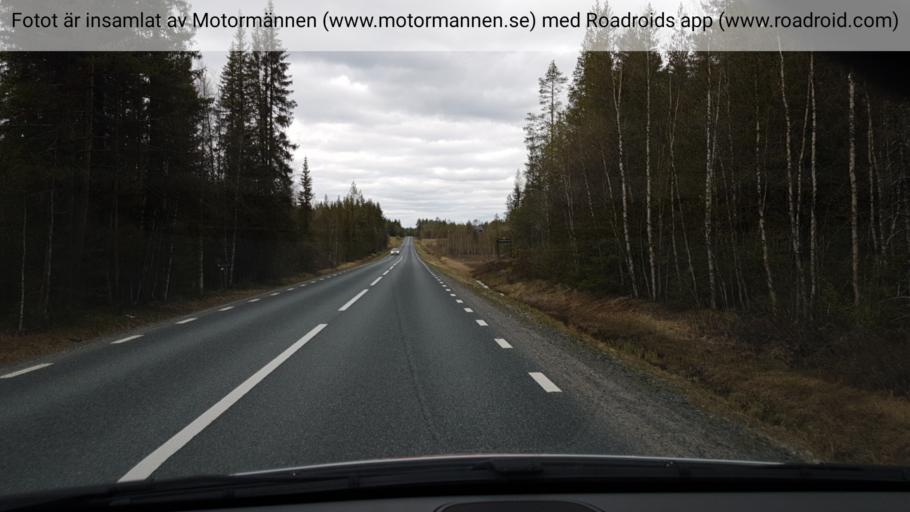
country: SE
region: Vaesterbotten
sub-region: Sorsele Kommun
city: Sorsele
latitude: 65.3843
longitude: 17.5780
